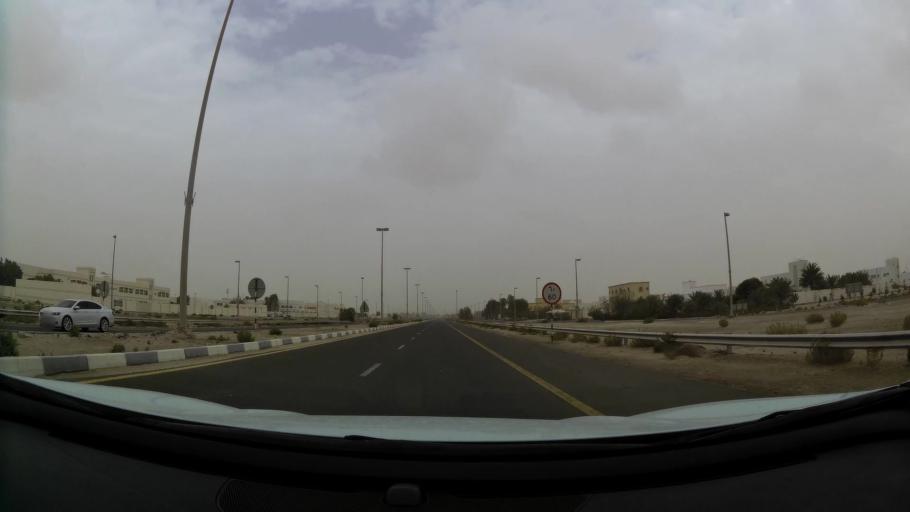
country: AE
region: Abu Dhabi
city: Abu Dhabi
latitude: 24.4040
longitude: 54.7343
